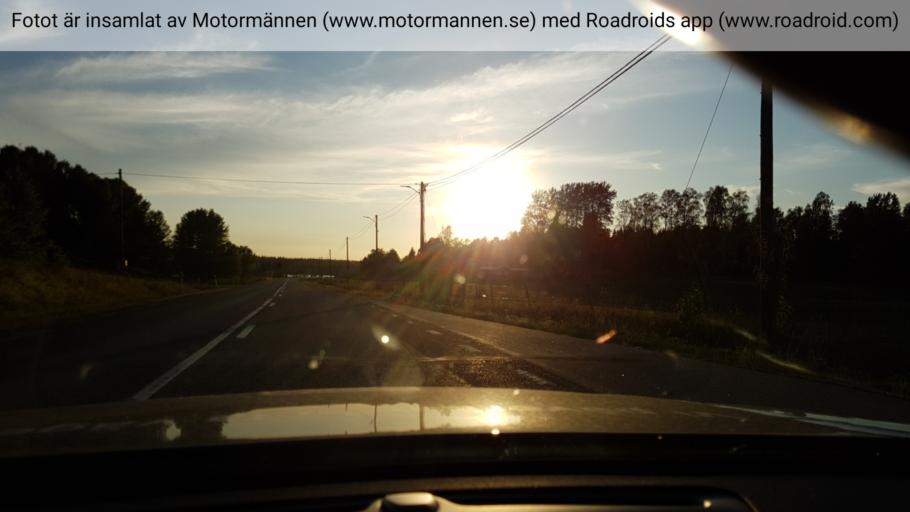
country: SE
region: OErebro
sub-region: Karlskoga Kommun
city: Karlskoga
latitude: 59.3927
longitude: 14.4607
